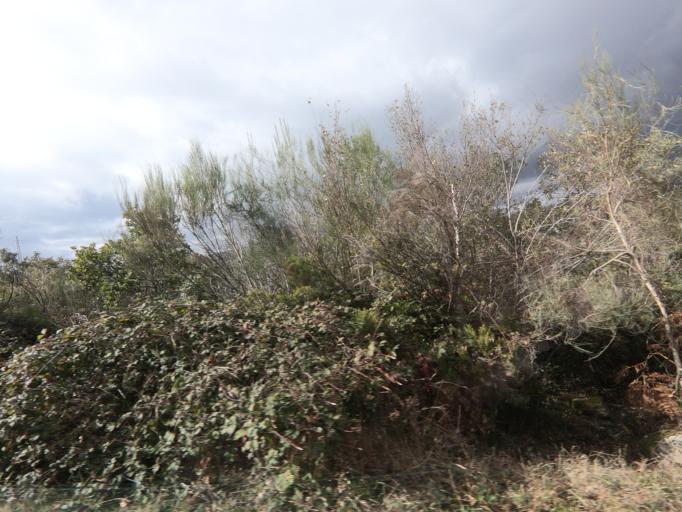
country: PT
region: Vila Real
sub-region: Vila Real
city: Vila Real
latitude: 41.3640
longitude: -7.7938
